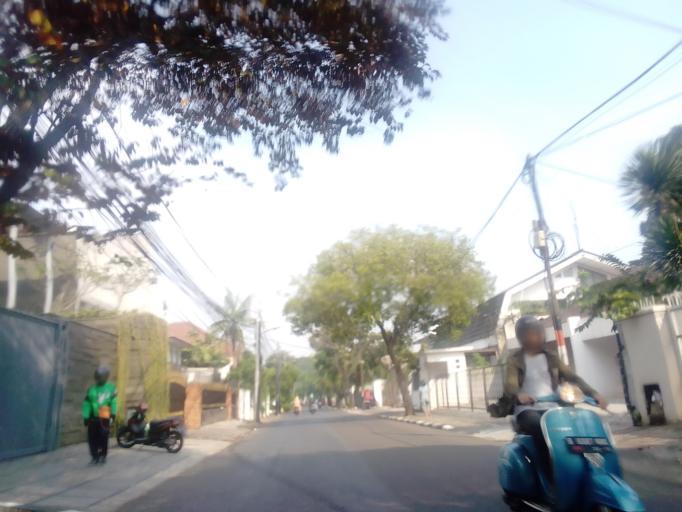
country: ID
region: Jakarta Raya
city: Jakarta
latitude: -6.2574
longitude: 106.8025
